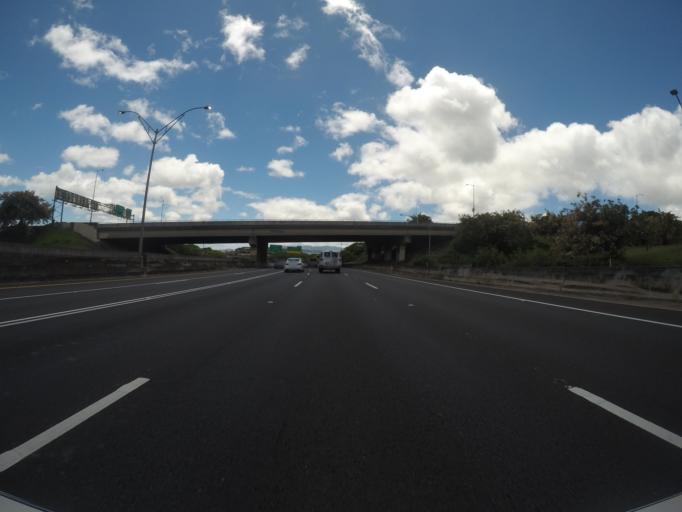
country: US
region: Hawaii
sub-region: Honolulu County
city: Halawa
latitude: 21.3722
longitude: -157.9189
